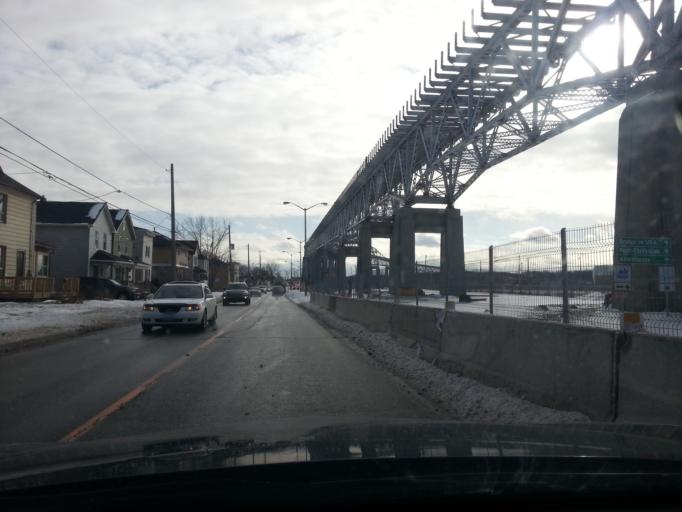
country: CA
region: Ontario
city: Cornwall
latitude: 45.0172
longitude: -74.7431
